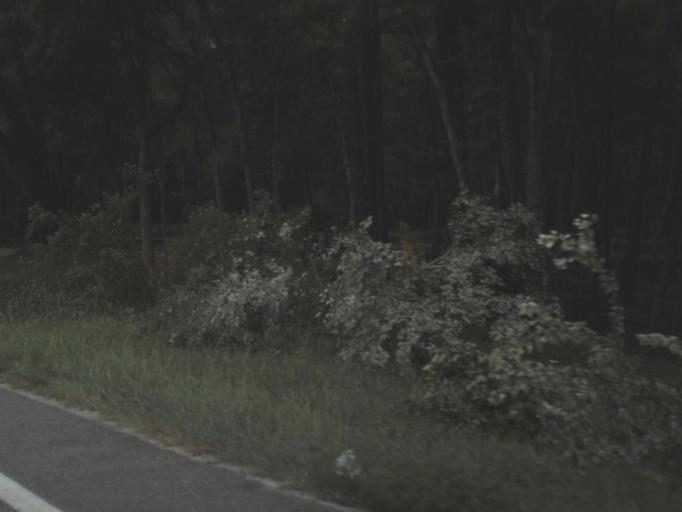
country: US
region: Florida
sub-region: Hamilton County
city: Jasper
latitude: 30.5242
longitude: -82.9921
